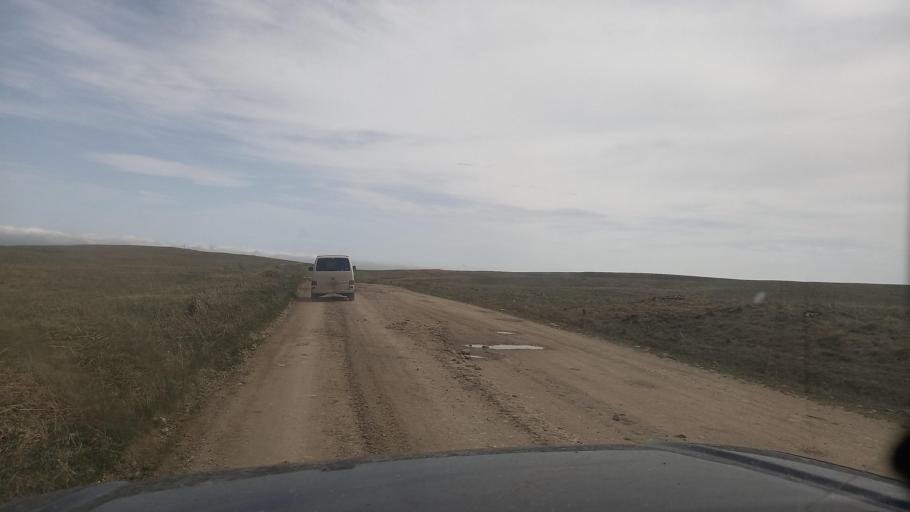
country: RU
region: Stavropol'skiy
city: Kislovodsk
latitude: 43.7532
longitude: 42.7458
